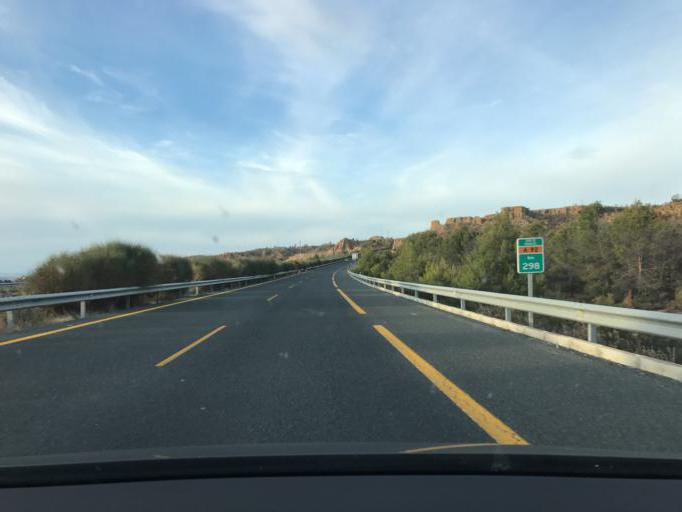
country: ES
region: Andalusia
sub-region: Provincia de Granada
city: Guadix
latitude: 37.3053
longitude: -3.1116
